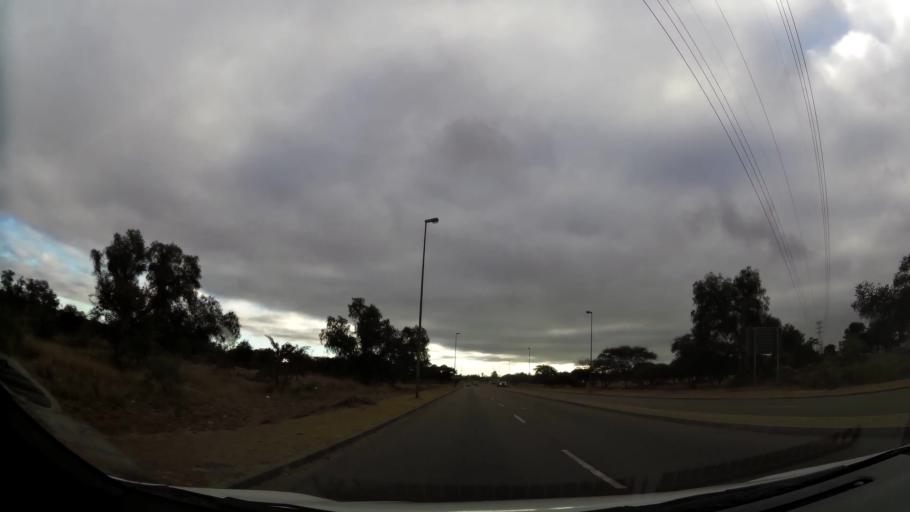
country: ZA
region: Limpopo
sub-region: Capricorn District Municipality
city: Polokwane
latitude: -23.8854
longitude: 29.4311
